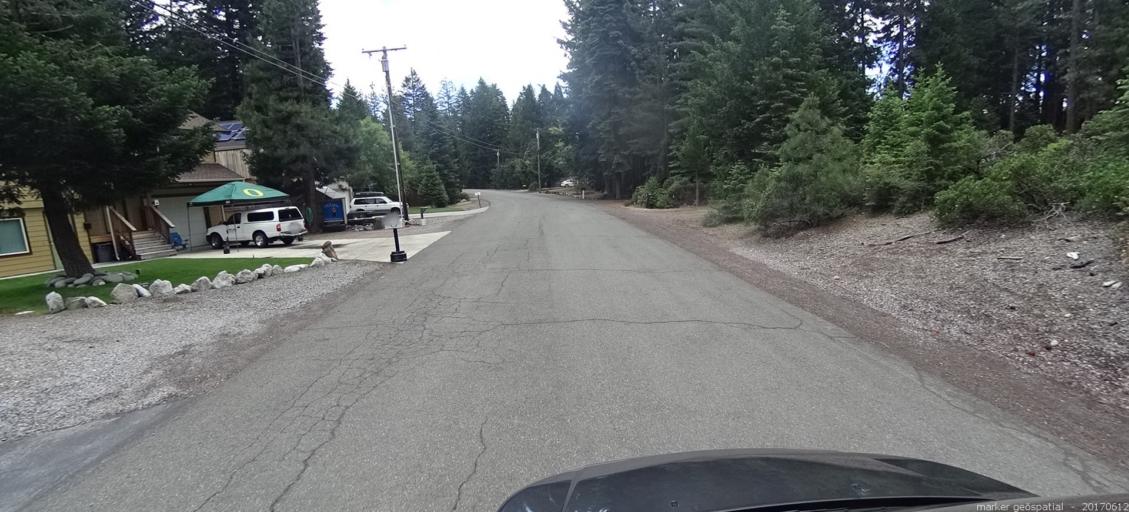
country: US
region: California
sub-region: Siskiyou County
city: Mount Shasta
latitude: 41.3465
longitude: -122.3562
